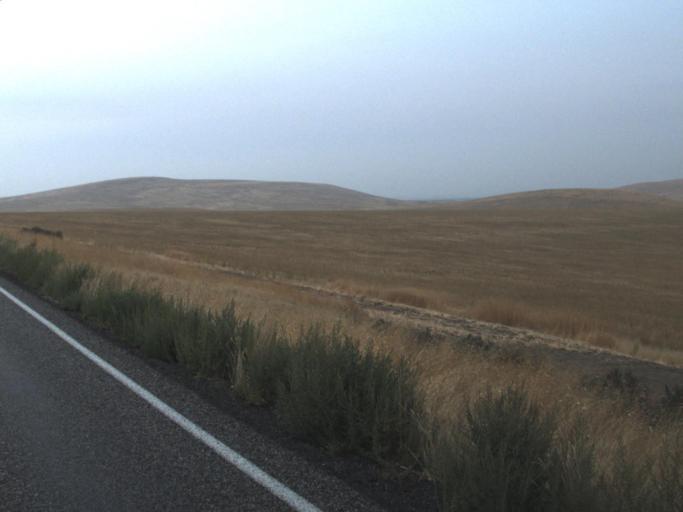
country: US
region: Washington
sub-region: Yakima County
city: Sunnyside
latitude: 46.4270
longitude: -119.9411
